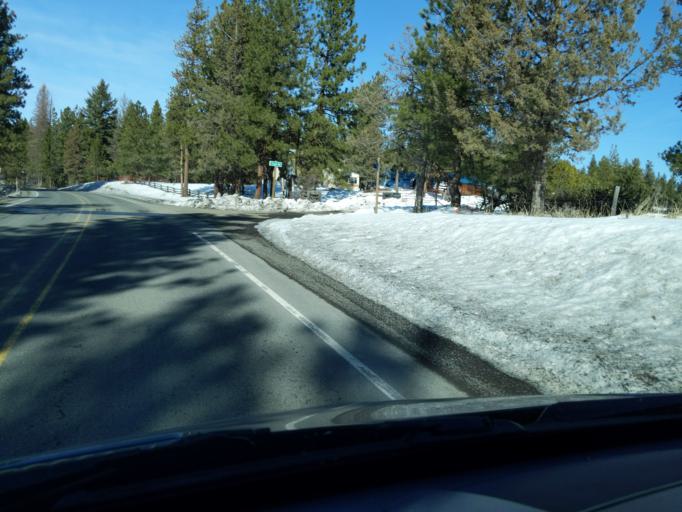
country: US
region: Oregon
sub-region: Grant County
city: John Day
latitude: 44.9139
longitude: -119.0087
